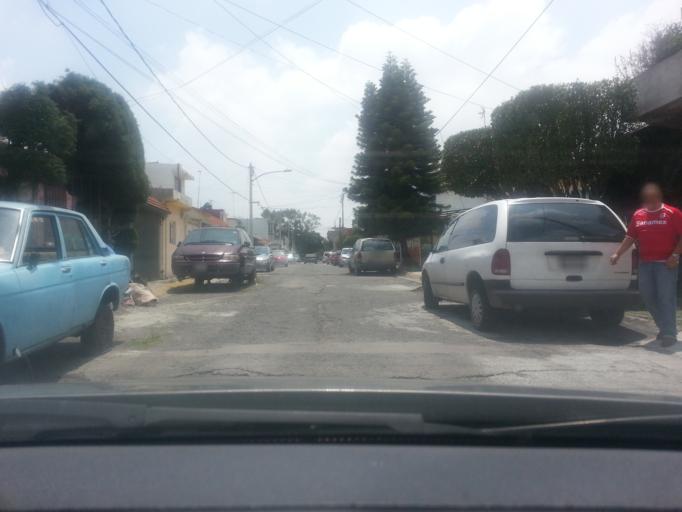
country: MX
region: Mexico
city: Cuautitlan Izcalli
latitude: 19.6487
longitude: -99.2174
